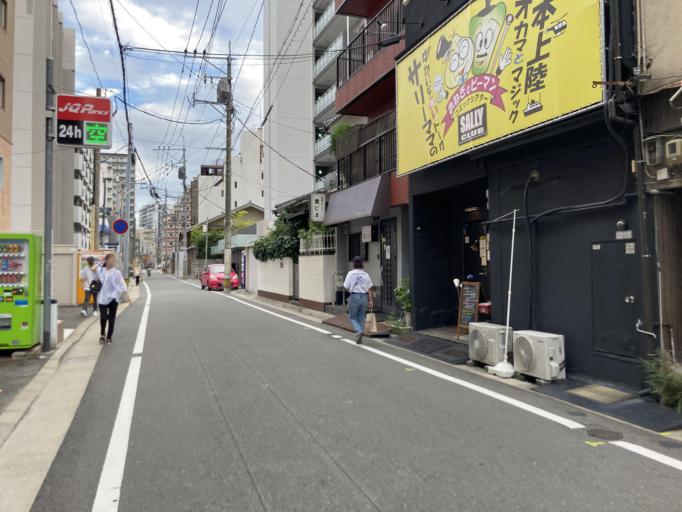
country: JP
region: Fukuoka
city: Fukuoka-shi
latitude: 33.5869
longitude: 130.4102
